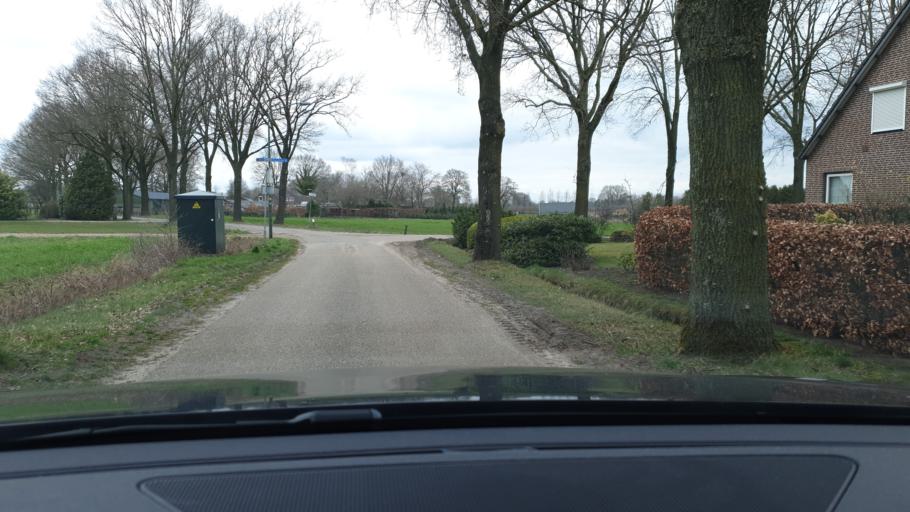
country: NL
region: North Brabant
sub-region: Gemeente Veldhoven
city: Oerle
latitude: 51.4320
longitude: 5.3379
